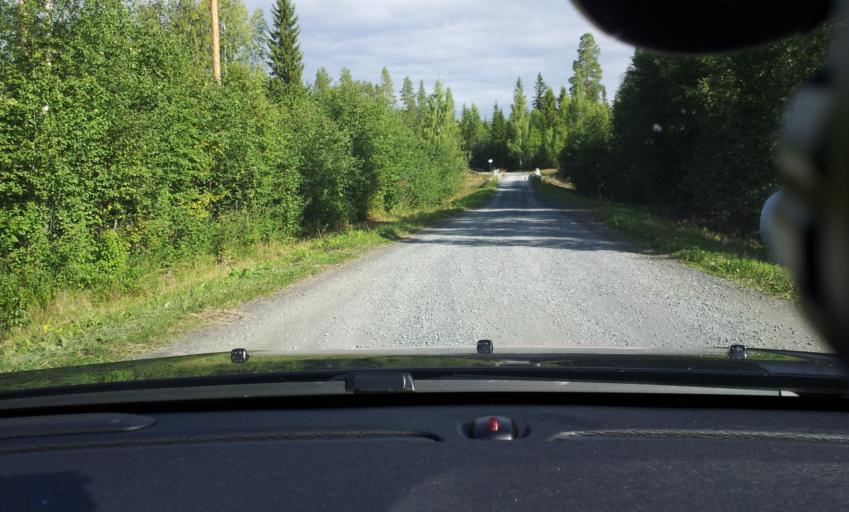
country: SE
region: Jaemtland
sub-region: Krokoms Kommun
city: Valla
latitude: 63.2637
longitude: 13.7875
